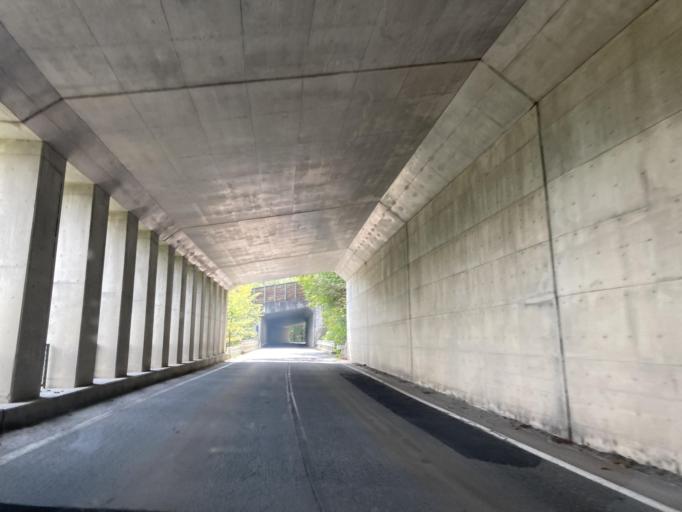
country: JP
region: Nagano
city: Omachi
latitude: 36.5237
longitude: 137.7906
